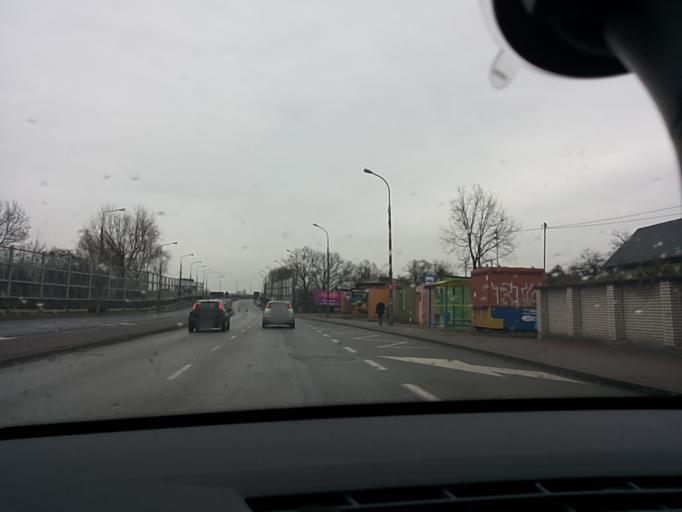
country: PL
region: Lodz Voivodeship
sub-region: Skierniewice
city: Skierniewice
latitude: 51.9704
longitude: 20.1476
